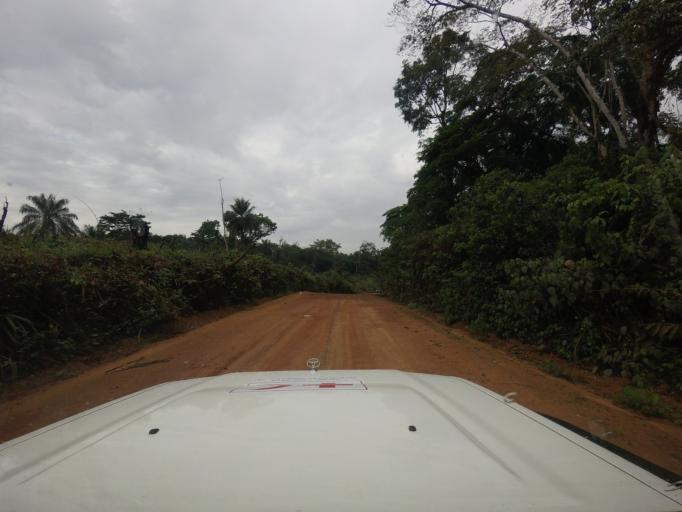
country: SL
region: Eastern Province
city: Buedu
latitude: 8.3307
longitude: -10.1642
